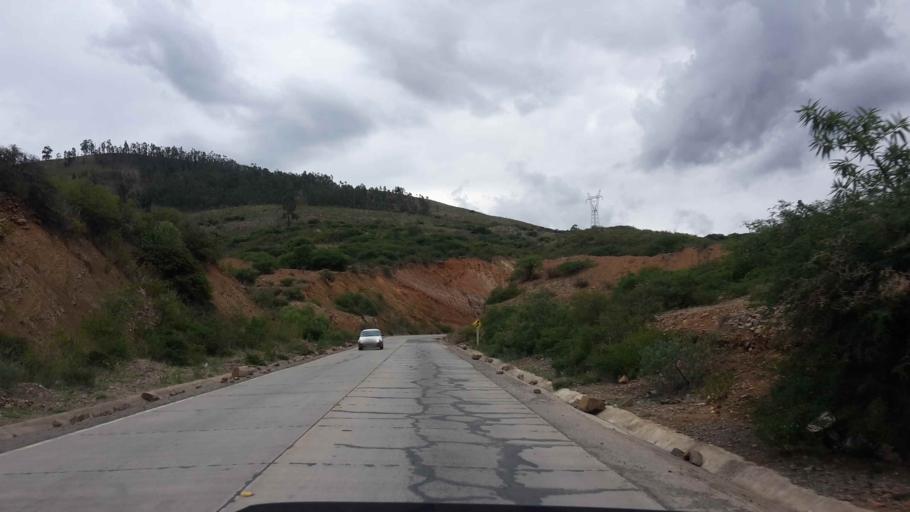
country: BO
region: Cochabamba
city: Cochabamba
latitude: -17.5321
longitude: -66.2015
